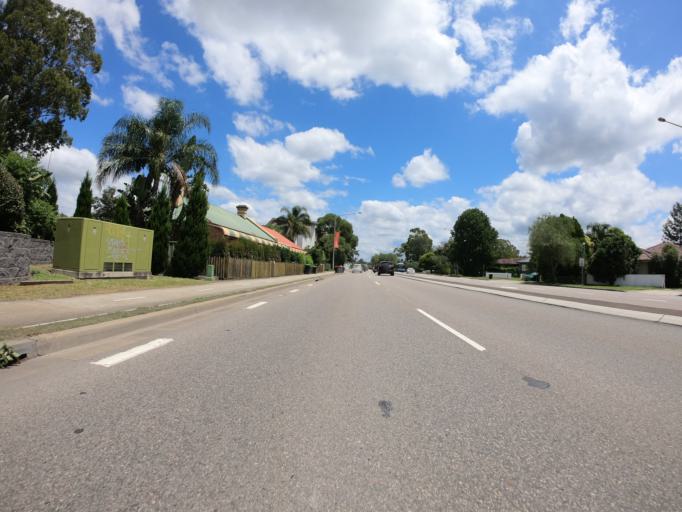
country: AU
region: New South Wales
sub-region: Penrith Municipality
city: Penrith
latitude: -33.7618
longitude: 150.6836
